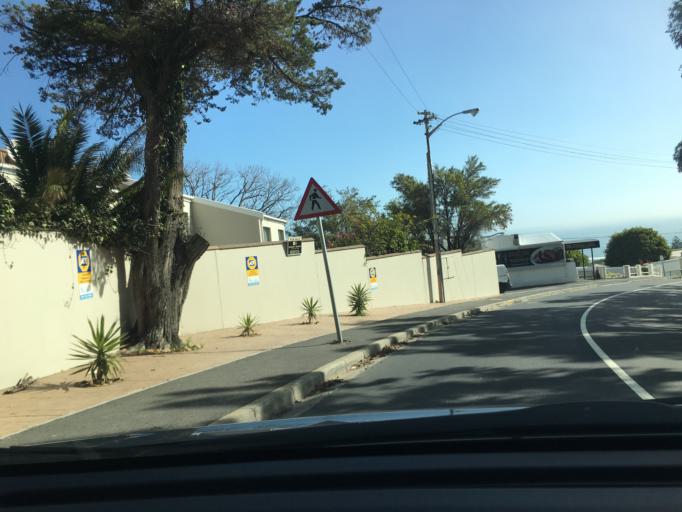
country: ZA
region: Western Cape
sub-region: City of Cape Town
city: Cape Town
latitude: -33.9631
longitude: 18.3786
